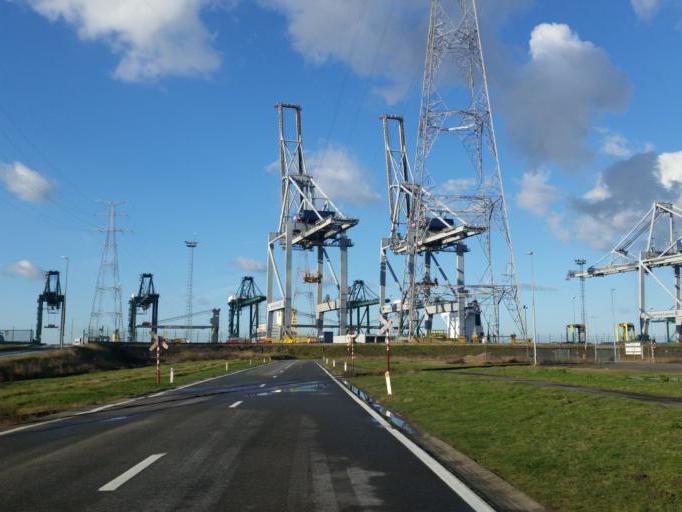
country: BE
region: Flanders
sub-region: Provincie Oost-Vlaanderen
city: Beveren
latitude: 51.2922
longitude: 4.2698
